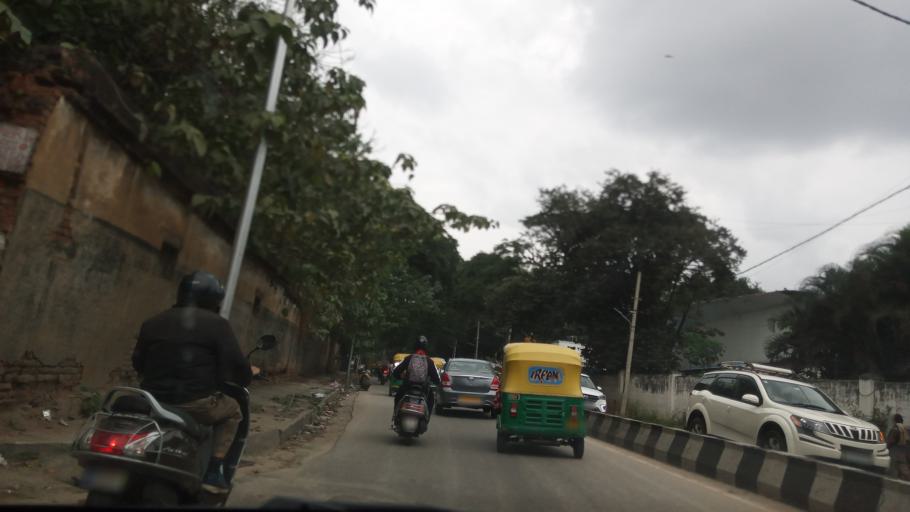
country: IN
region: Karnataka
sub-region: Bangalore Urban
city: Bangalore
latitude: 12.9961
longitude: 77.5959
